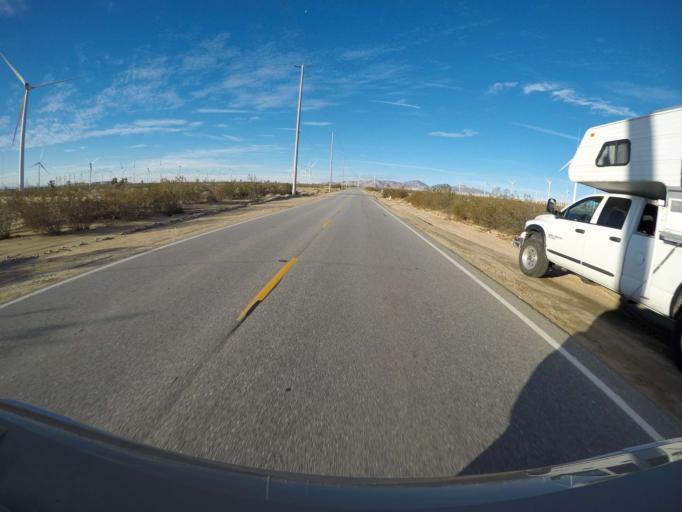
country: US
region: California
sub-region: Kern County
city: Mojave
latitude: 35.0423
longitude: -118.2322
